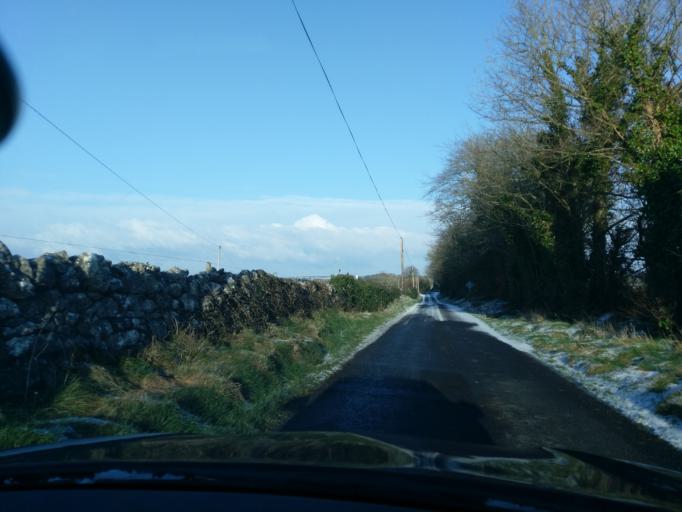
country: IE
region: Connaught
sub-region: County Galway
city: Athenry
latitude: 53.1749
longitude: -8.7437
